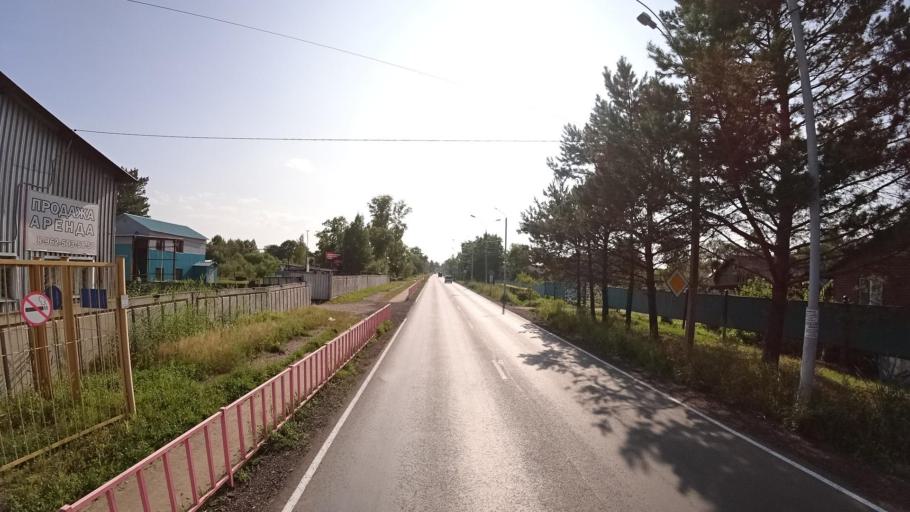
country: RU
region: Khabarovsk Krai
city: Khor
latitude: 47.9741
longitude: 135.0654
